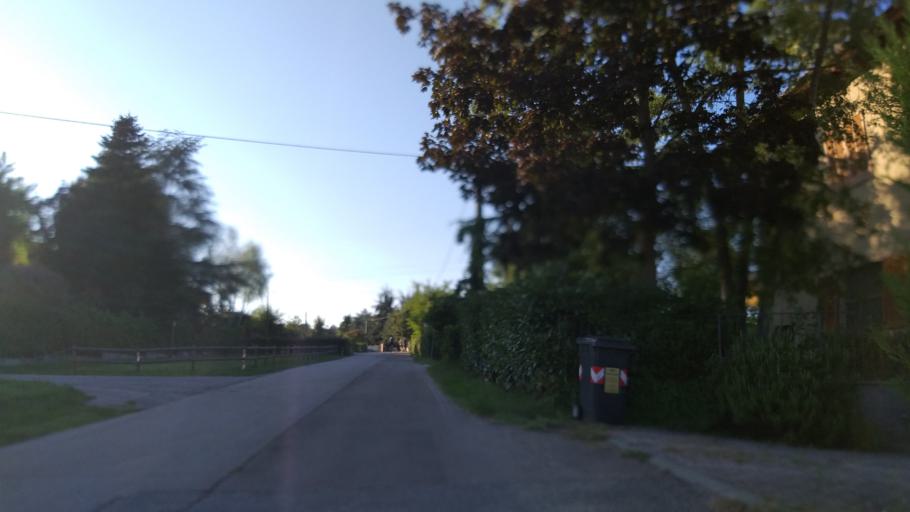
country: IT
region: Piedmont
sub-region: Provincia di Asti
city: Asti
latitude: 44.9234
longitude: 8.1990
